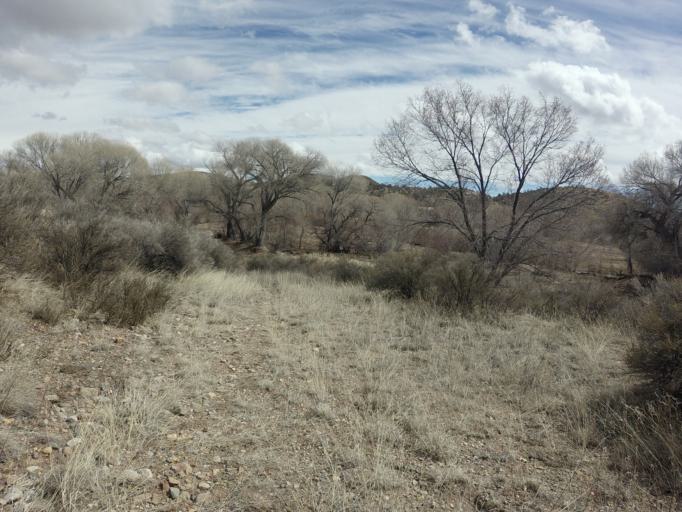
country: US
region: Arizona
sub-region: Yavapai County
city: Prescott
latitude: 34.5770
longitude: -112.4315
